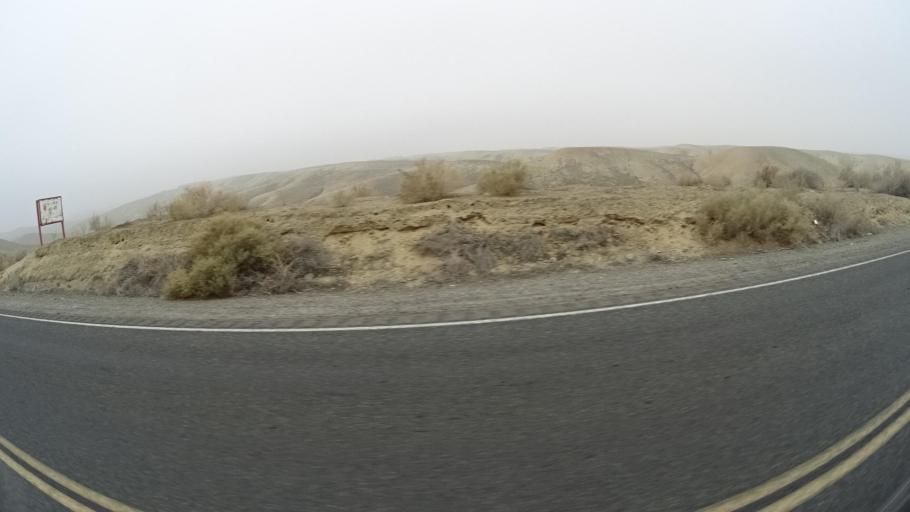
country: US
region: California
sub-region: Kern County
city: Buttonwillow
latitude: 35.3249
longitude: -119.4662
